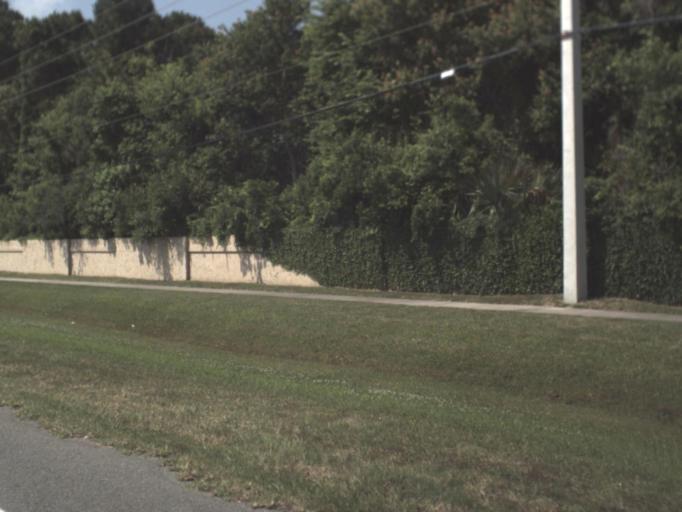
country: US
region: Florida
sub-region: Saint Johns County
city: Ponte Vedra Beach
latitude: 30.2210
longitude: -81.3832
